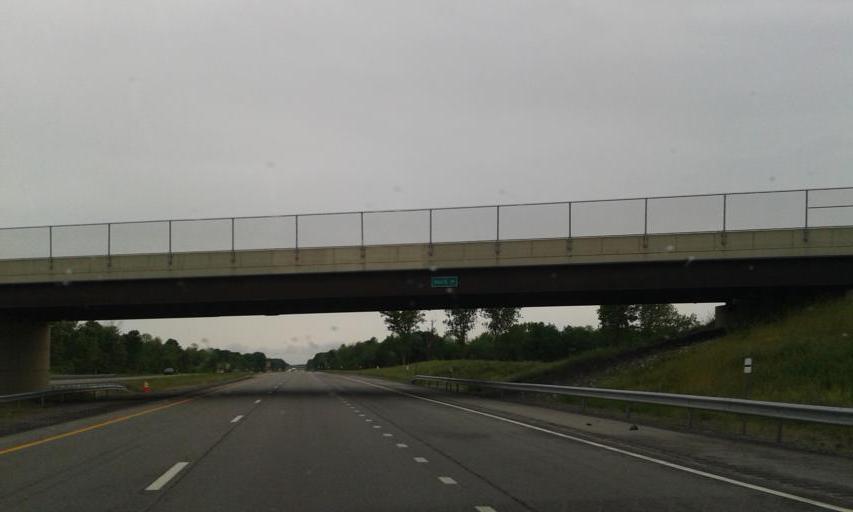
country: US
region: New York
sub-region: Genesee County
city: Le Roy
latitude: 43.0292
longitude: -77.9696
